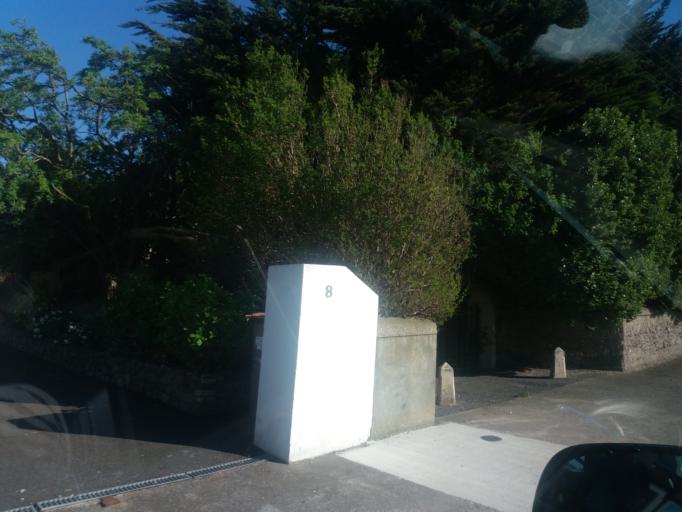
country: IE
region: Leinster
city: Sutton
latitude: 53.3825
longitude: -6.1017
